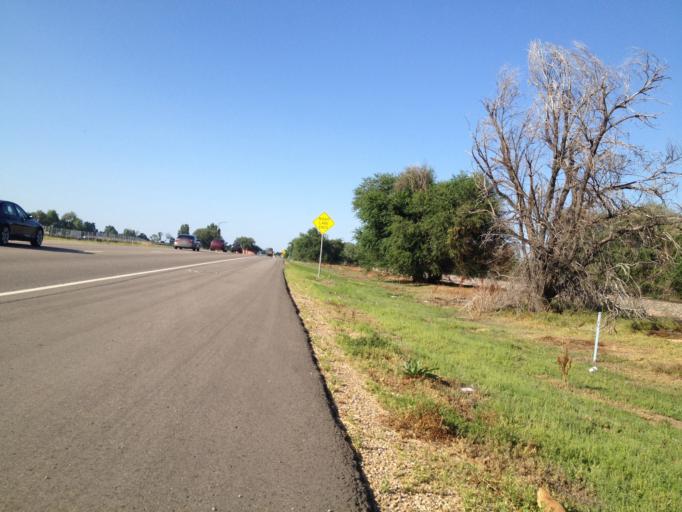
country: US
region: Colorado
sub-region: Boulder County
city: Boulder
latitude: 40.0412
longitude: -105.2415
